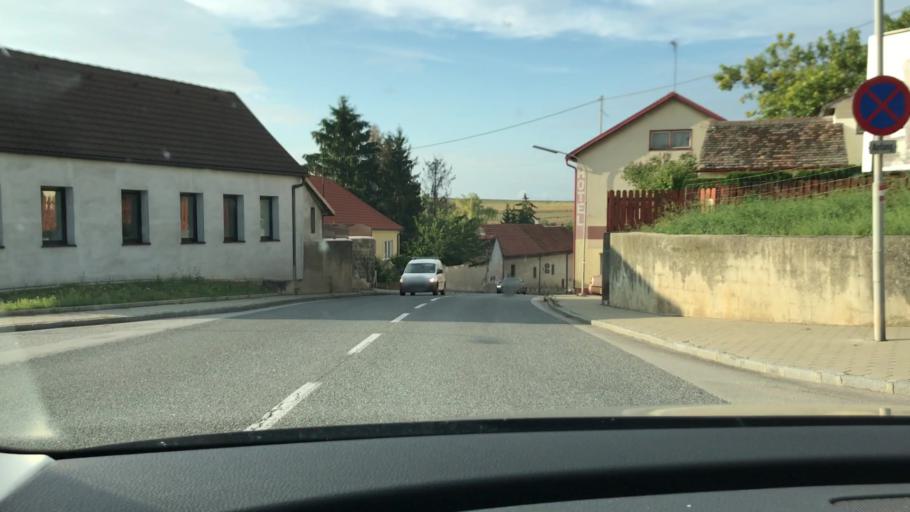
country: AT
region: Lower Austria
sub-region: Politischer Bezirk Mistelbach
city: Drasenhofen
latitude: 48.7548
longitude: 16.6473
